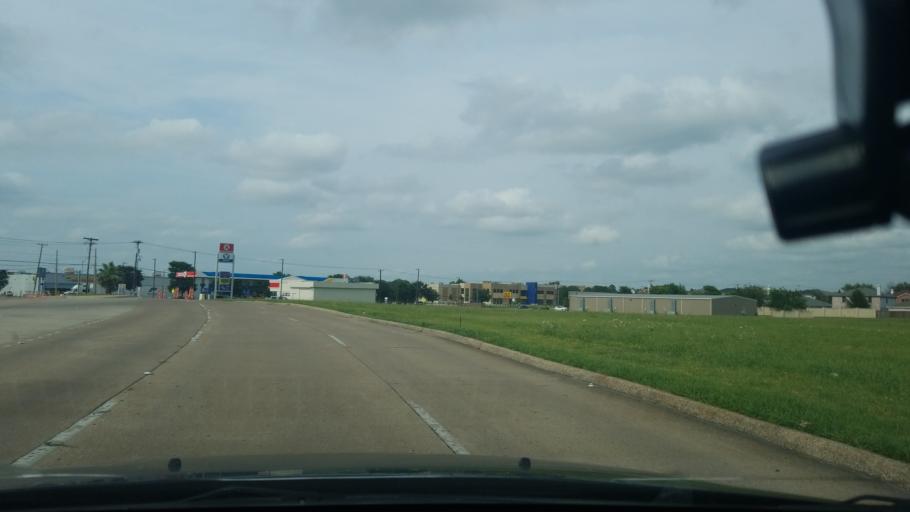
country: US
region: Texas
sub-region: Dallas County
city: Balch Springs
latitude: 32.7668
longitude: -96.6469
